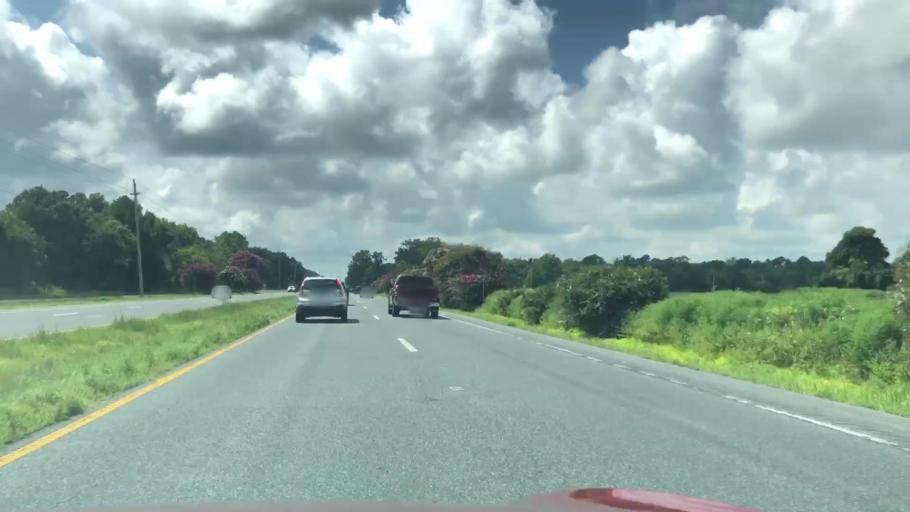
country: US
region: Virginia
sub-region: Northampton County
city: Exmore
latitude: 37.4604
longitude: -75.8685
